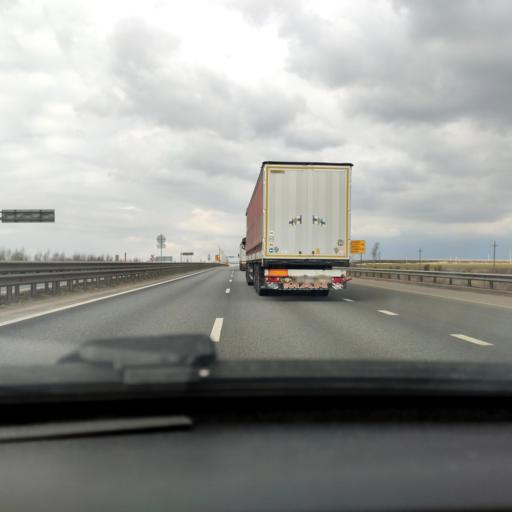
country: RU
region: Tula
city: Kazachka
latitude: 53.3636
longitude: 38.1831
